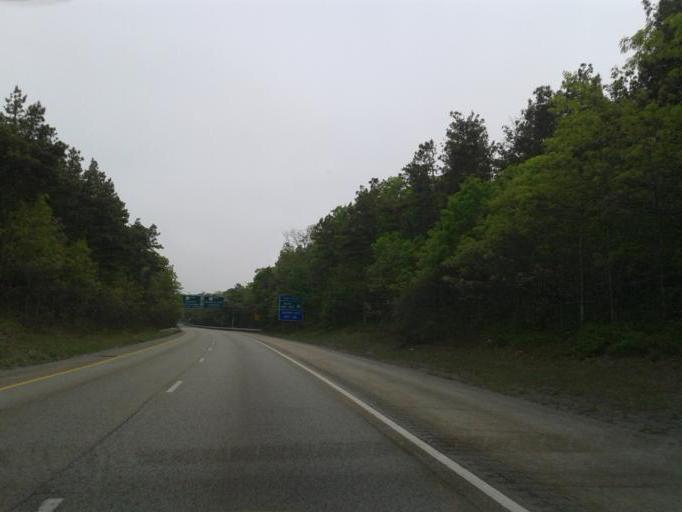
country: US
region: Massachusetts
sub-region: Barnstable County
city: Sagamore
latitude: 41.7895
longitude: -70.5456
